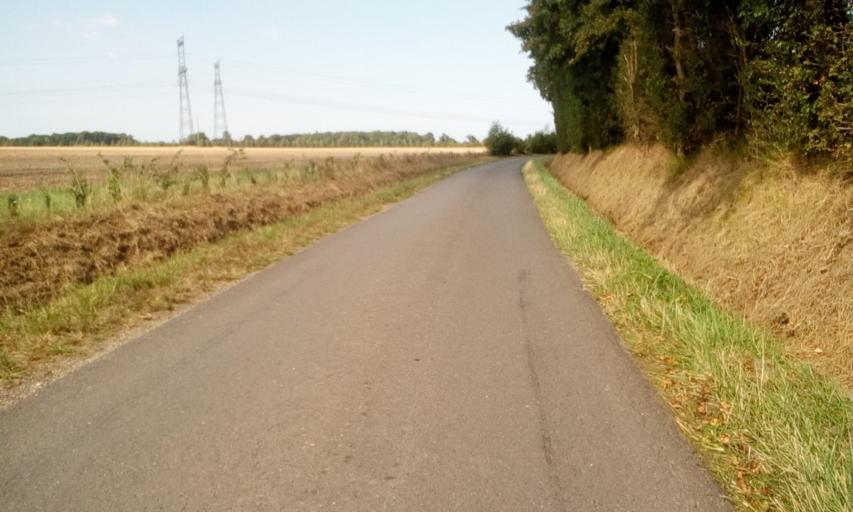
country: FR
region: Lower Normandy
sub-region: Departement du Calvados
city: Argences
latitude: 49.1469
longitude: -0.1255
